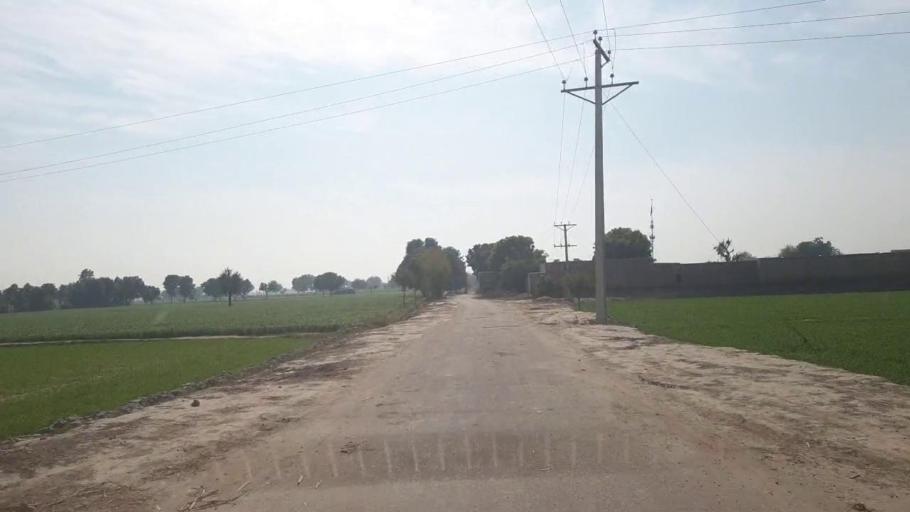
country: PK
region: Sindh
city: Shahpur Chakar
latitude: 26.1507
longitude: 68.5111
